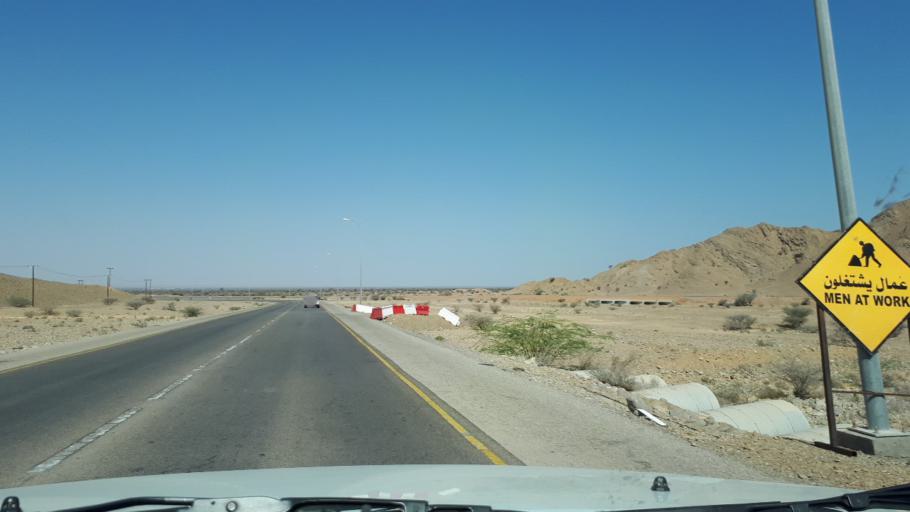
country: OM
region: Ash Sharqiyah
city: Sur
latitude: 22.3156
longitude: 59.2990
